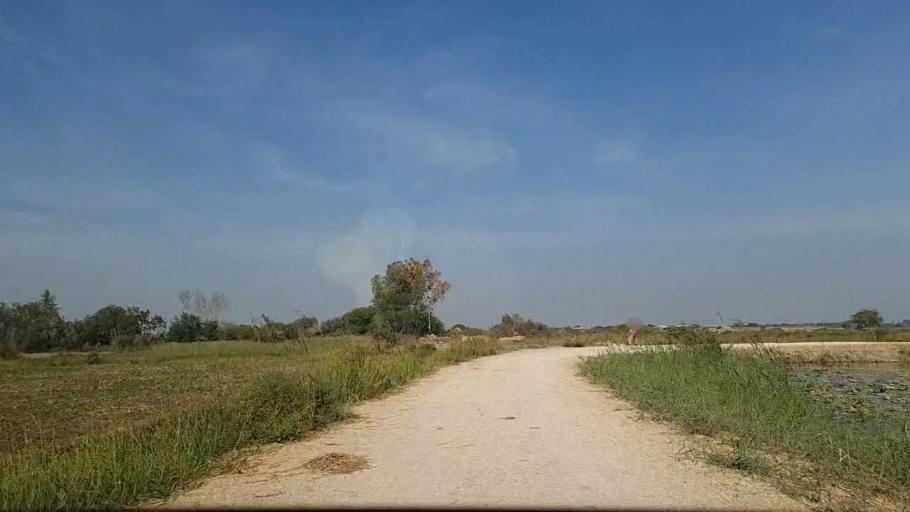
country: PK
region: Sindh
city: Daro Mehar
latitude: 24.7057
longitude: 68.1498
